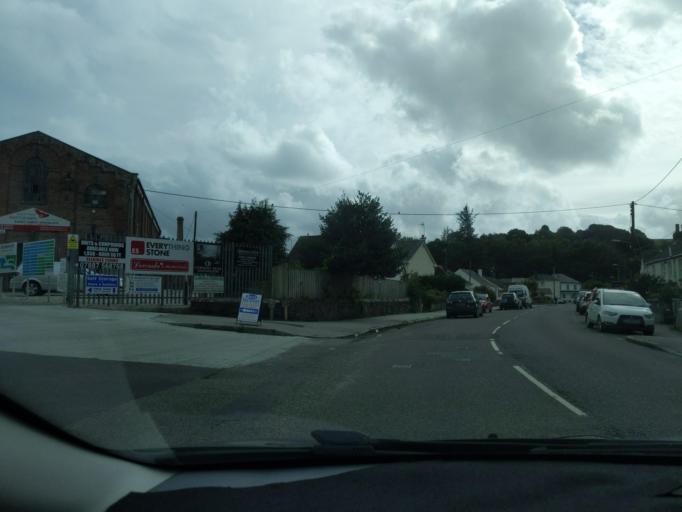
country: GB
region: England
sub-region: Cornwall
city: Par
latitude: 50.3523
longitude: -4.7106
